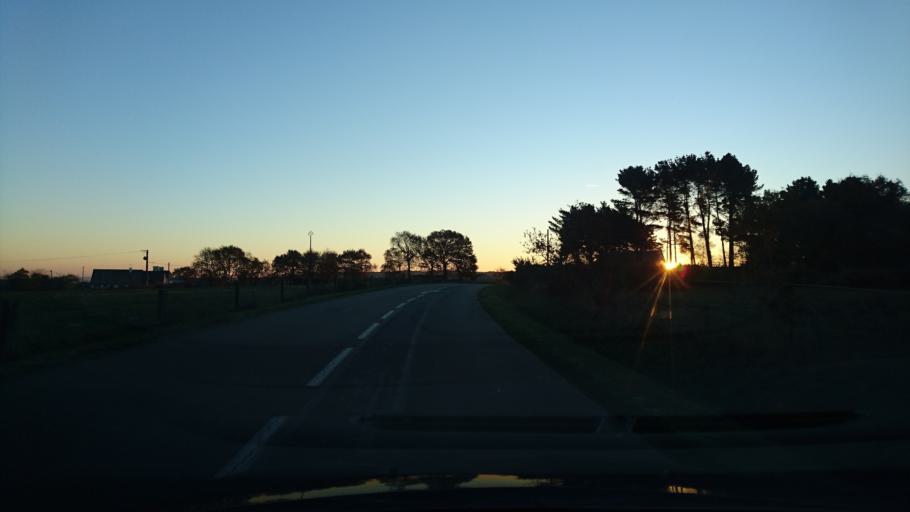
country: FR
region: Brittany
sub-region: Departement des Cotes-d'Armor
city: Saint-Julien
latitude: 48.4603
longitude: -2.7800
